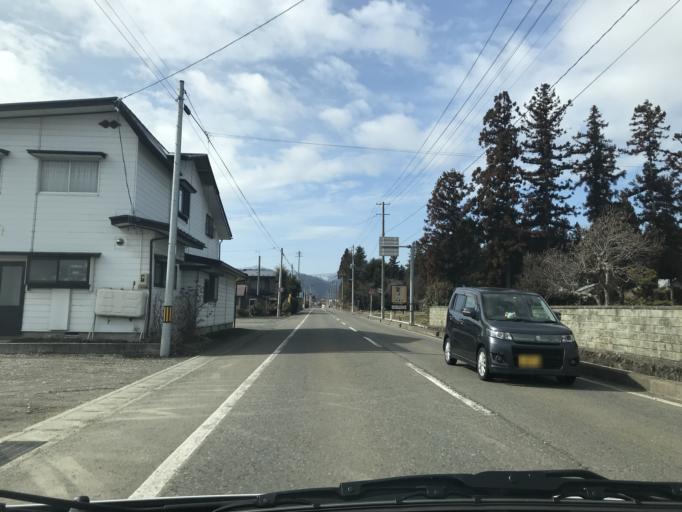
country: JP
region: Iwate
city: Hanamaki
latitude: 39.3907
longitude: 141.0518
